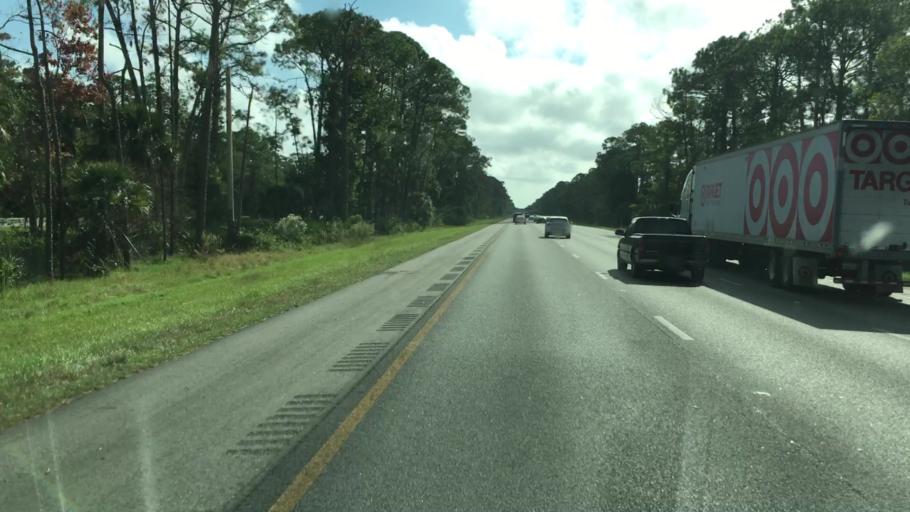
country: US
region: Florida
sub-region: Volusia County
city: Port Orange
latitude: 29.1272
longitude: -81.0563
